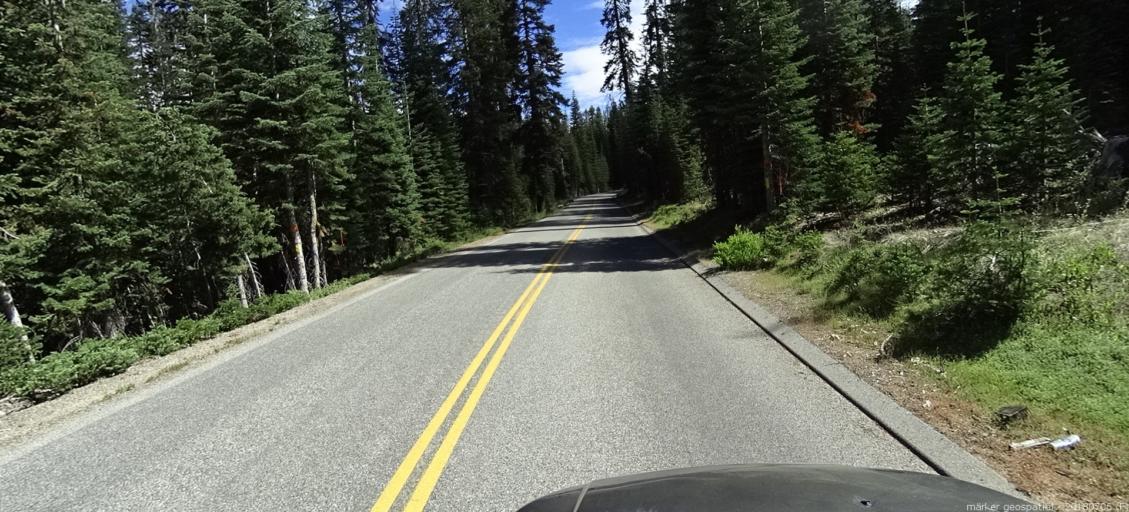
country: US
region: California
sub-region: Madera County
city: Oakhurst
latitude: 37.4120
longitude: -119.4980
